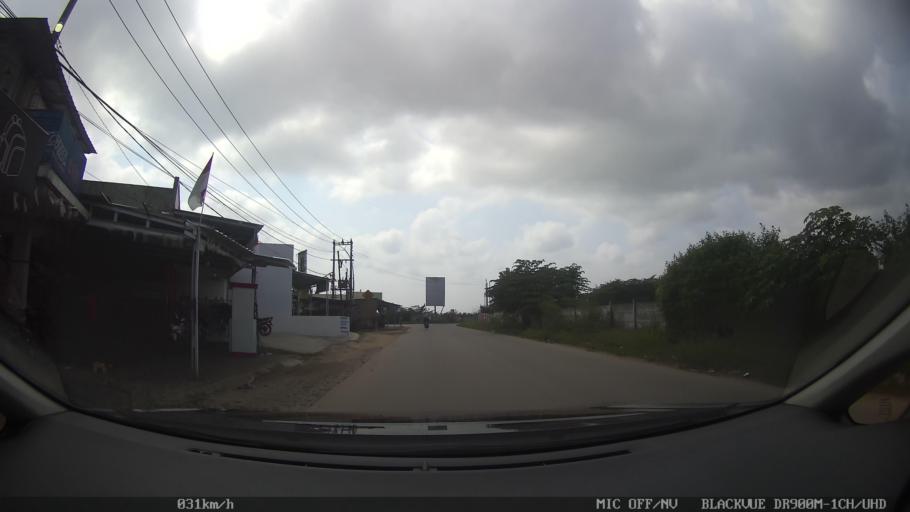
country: ID
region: Lampung
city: Kedaton
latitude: -5.3310
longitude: 105.2924
